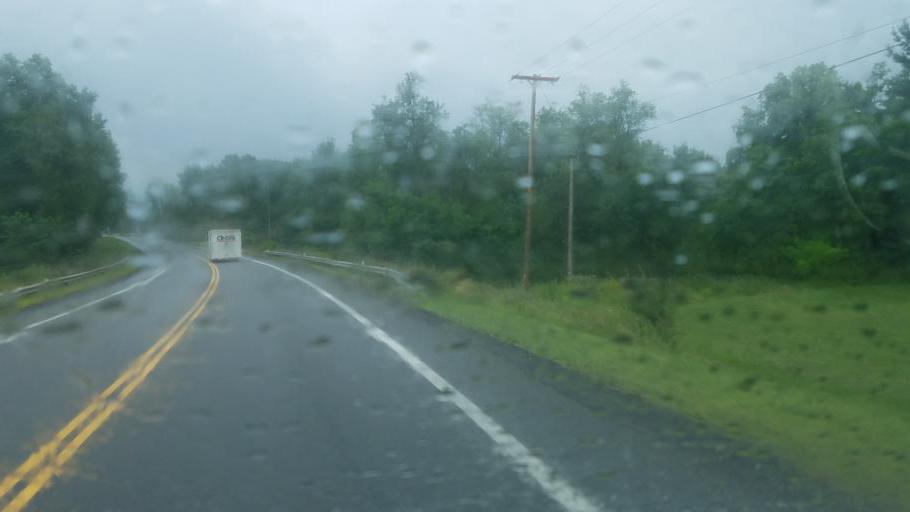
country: US
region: Ohio
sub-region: Trumbull County
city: Champion Heights
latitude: 41.3624
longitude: -80.8646
